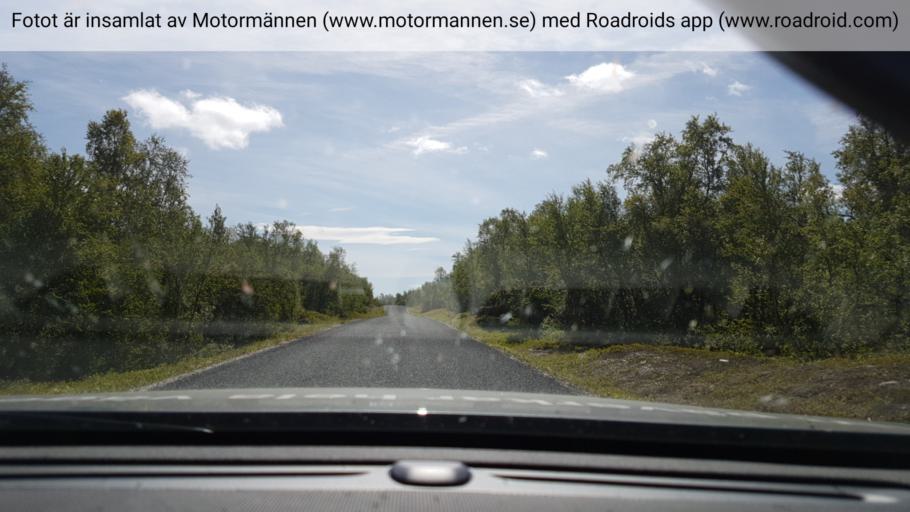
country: NO
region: Nordland
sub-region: Hattfjelldal
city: Hattfjelldal
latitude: 65.4065
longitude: 14.9472
